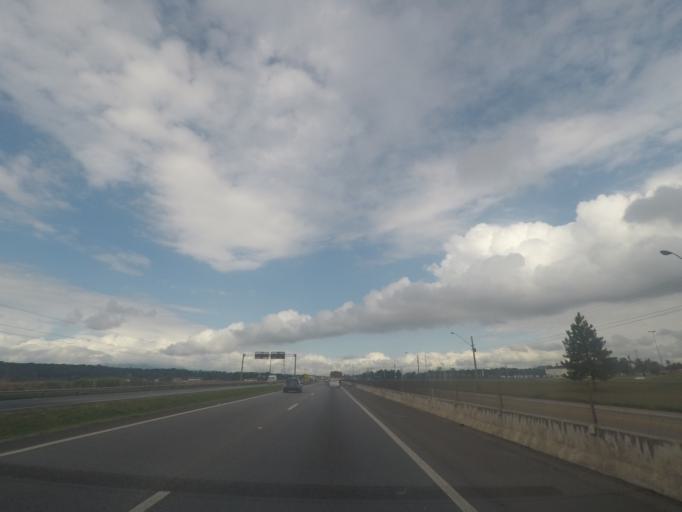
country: BR
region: Parana
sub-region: Piraquara
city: Piraquara
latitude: -25.5185
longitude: -49.1127
